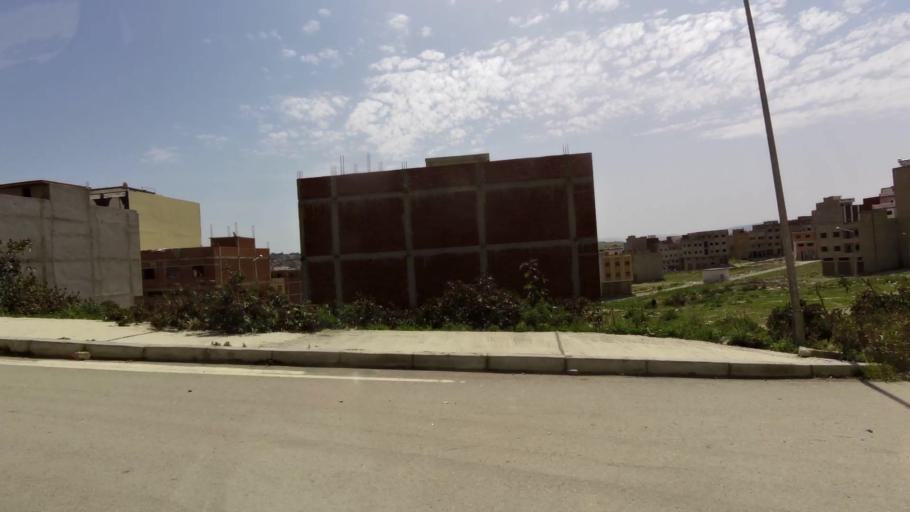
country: MA
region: Tanger-Tetouan
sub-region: Tanger-Assilah
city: Tangier
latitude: 35.7297
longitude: -5.8107
